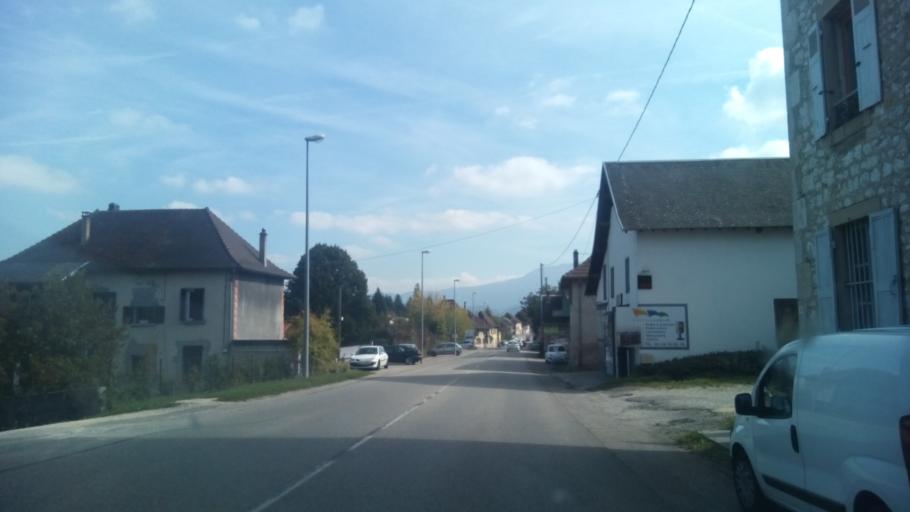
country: FR
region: Rhone-Alpes
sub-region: Departement de la Savoie
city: Le Pont-de-Beauvoisin
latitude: 45.5370
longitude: 5.6554
